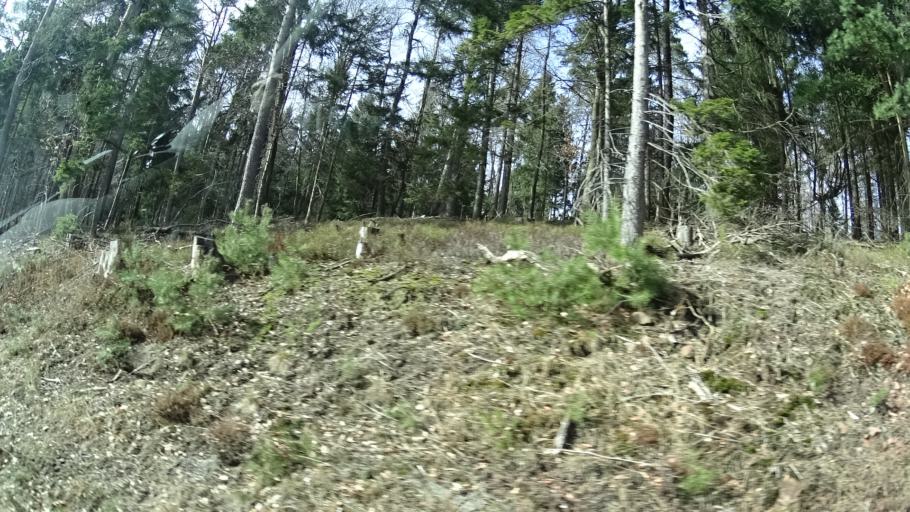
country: DE
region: Rheinland-Pfalz
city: Ramberg
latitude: 49.3001
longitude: 8.0355
